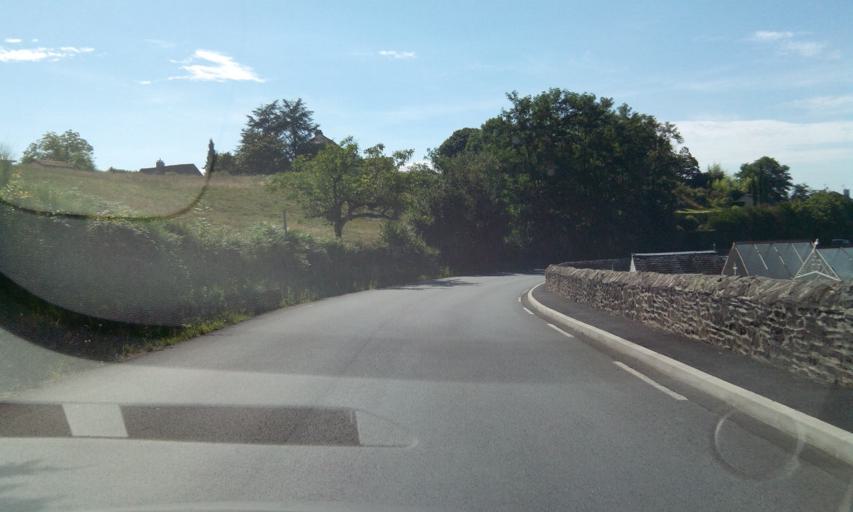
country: FR
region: Limousin
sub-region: Departement de la Correze
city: Beynat
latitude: 45.1238
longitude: 1.7288
